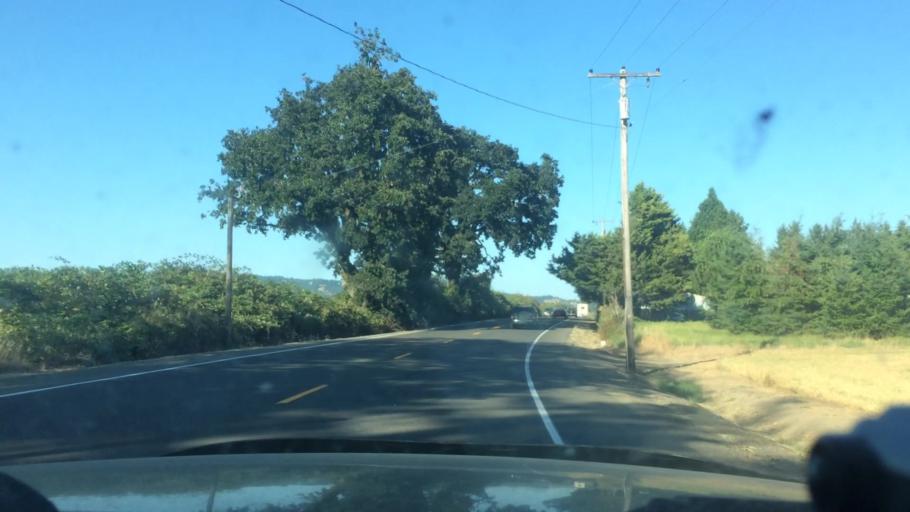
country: US
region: Oregon
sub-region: Yamhill County
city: Newberg
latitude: 45.2424
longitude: -122.9505
